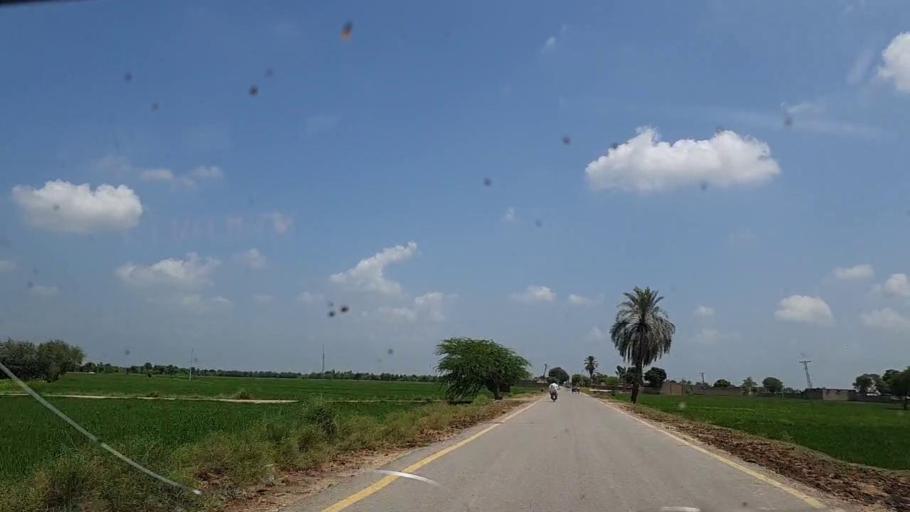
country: PK
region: Sindh
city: Tharu Shah
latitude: 26.9812
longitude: 68.0823
